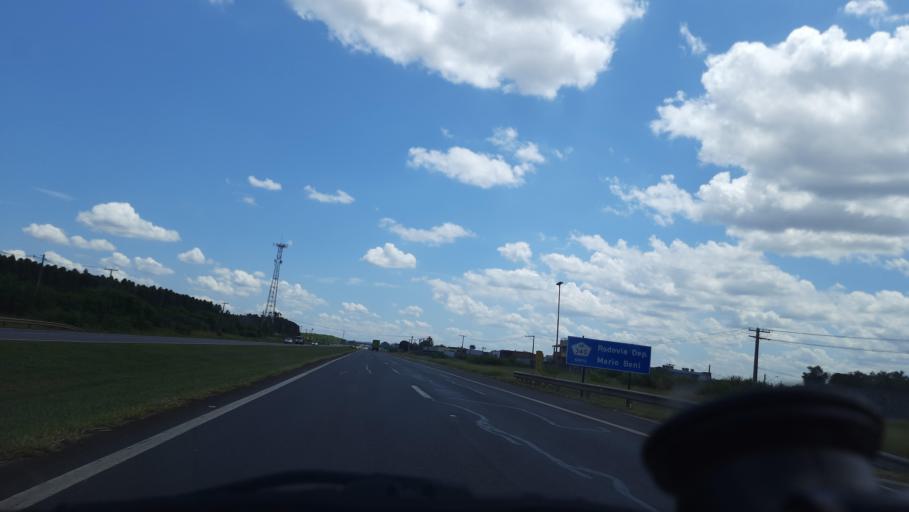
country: BR
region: Sao Paulo
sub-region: Moji-Guacu
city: Mogi-Gaucu
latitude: -22.3436
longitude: -46.9569
